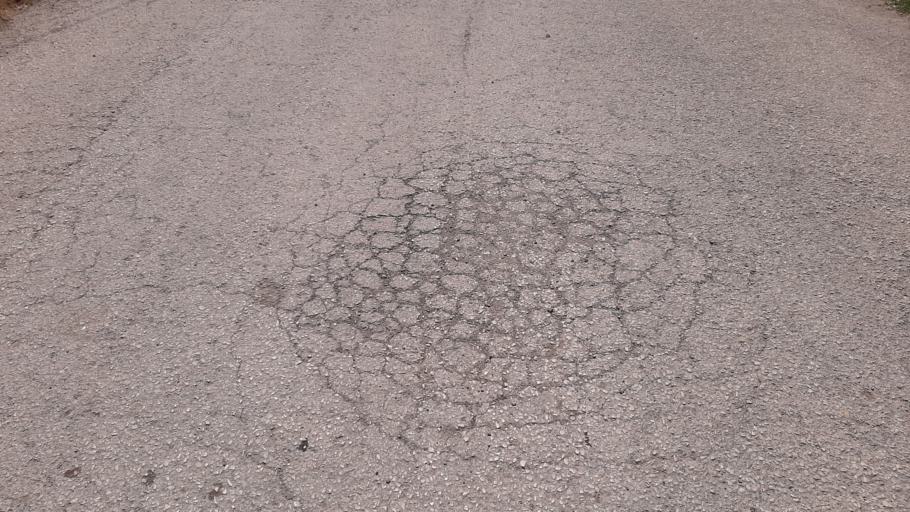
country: TN
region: Silyanah
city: Siliana
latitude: 36.0883
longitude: 9.3742
